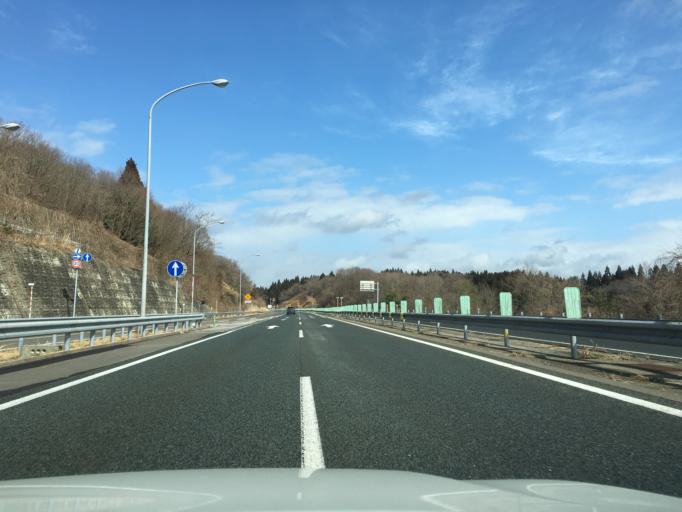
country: JP
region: Akita
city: Akita
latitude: 39.7231
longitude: 140.1812
